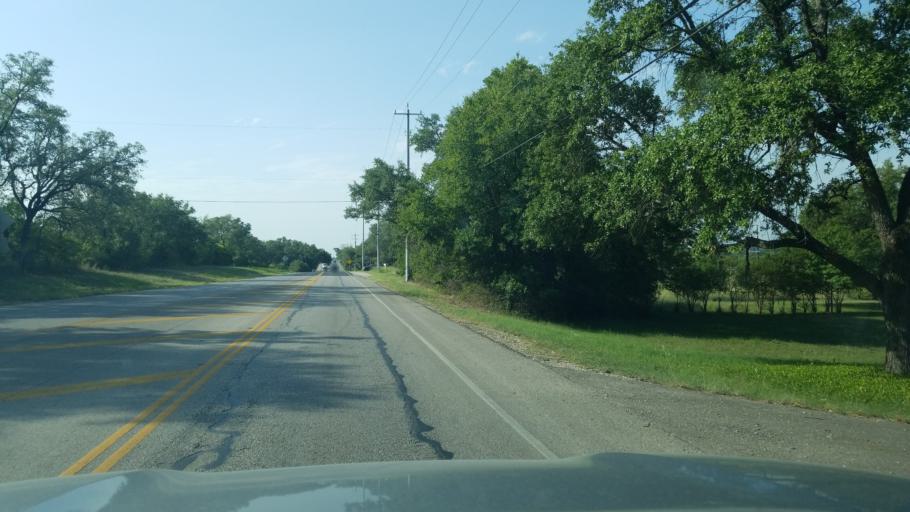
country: US
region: Texas
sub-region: Bexar County
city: Helotes
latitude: 29.4602
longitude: -98.7577
